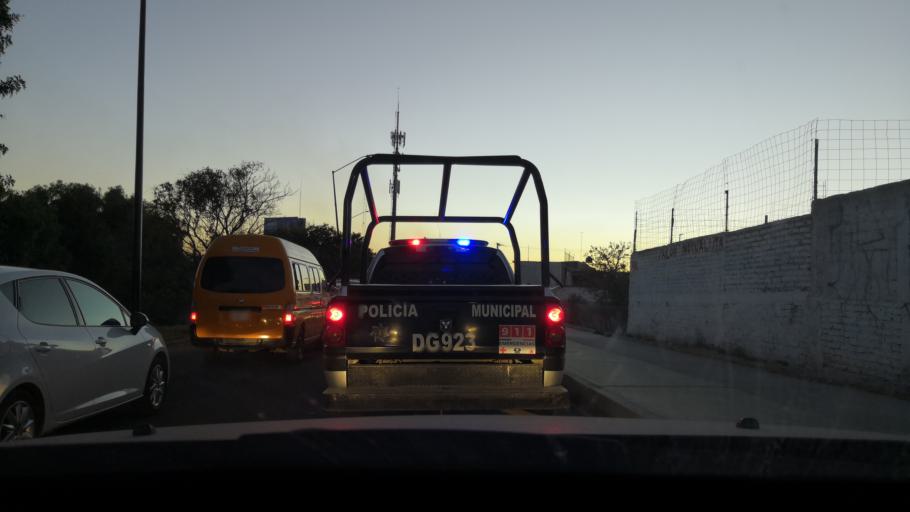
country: MX
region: Guanajuato
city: Leon
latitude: 21.0996
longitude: -101.6645
